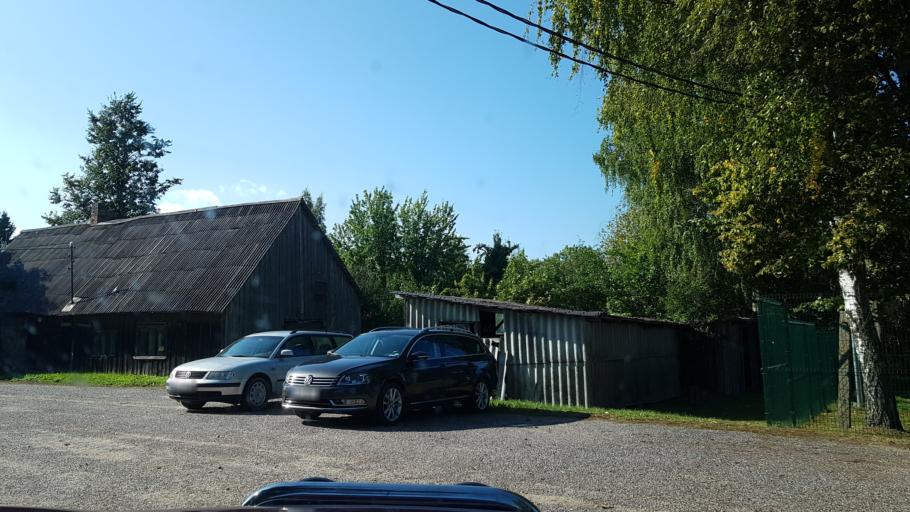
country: EE
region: Polvamaa
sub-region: Raepina vald
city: Rapina
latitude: 58.2333
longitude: 27.4755
